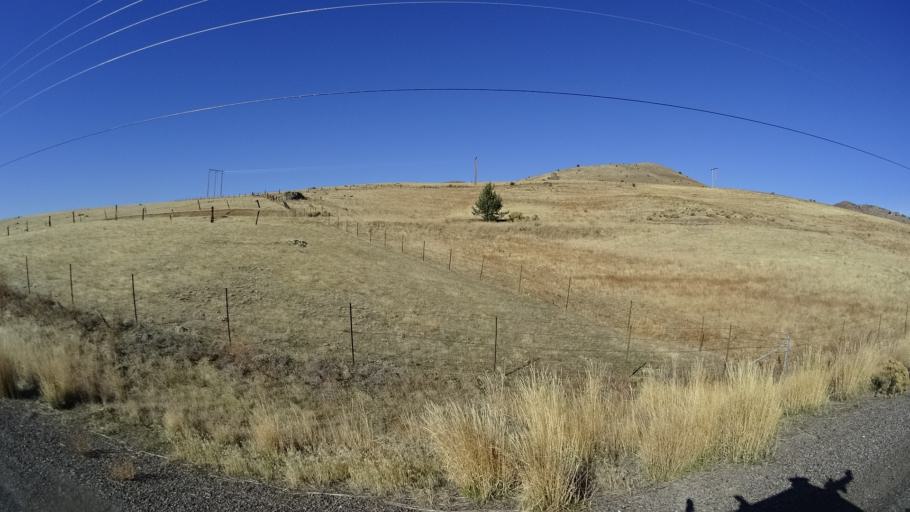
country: US
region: California
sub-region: Siskiyou County
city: Montague
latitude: 41.7779
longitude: -122.5228
